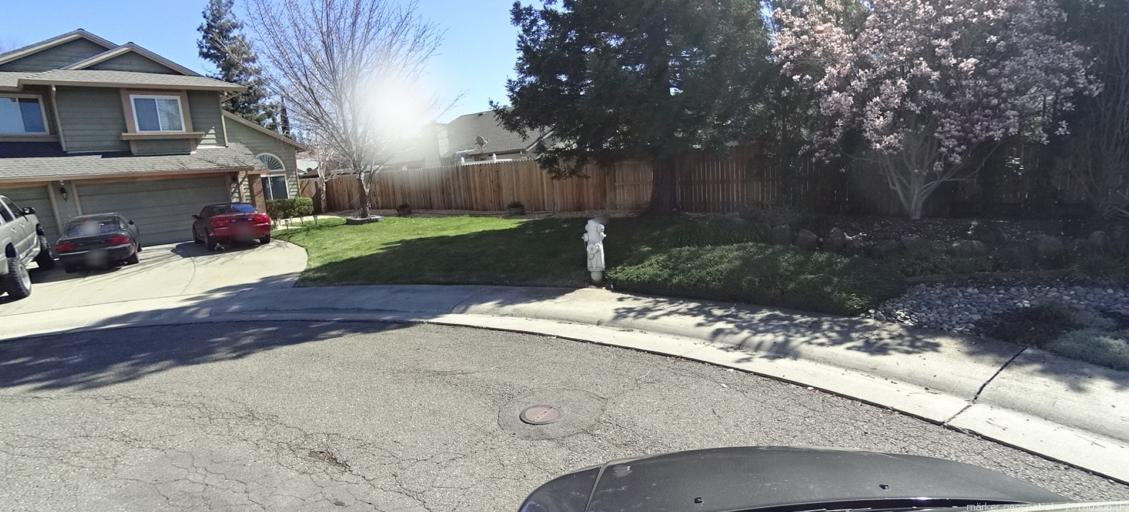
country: US
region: California
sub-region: Sacramento County
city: Vineyard
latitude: 38.4656
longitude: -121.3636
